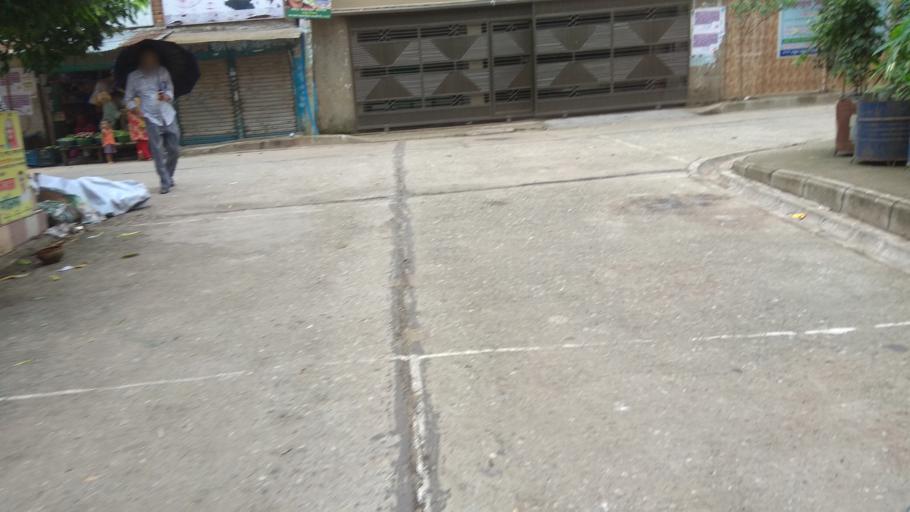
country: BD
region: Dhaka
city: Azimpur
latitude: 23.8060
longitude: 90.3575
